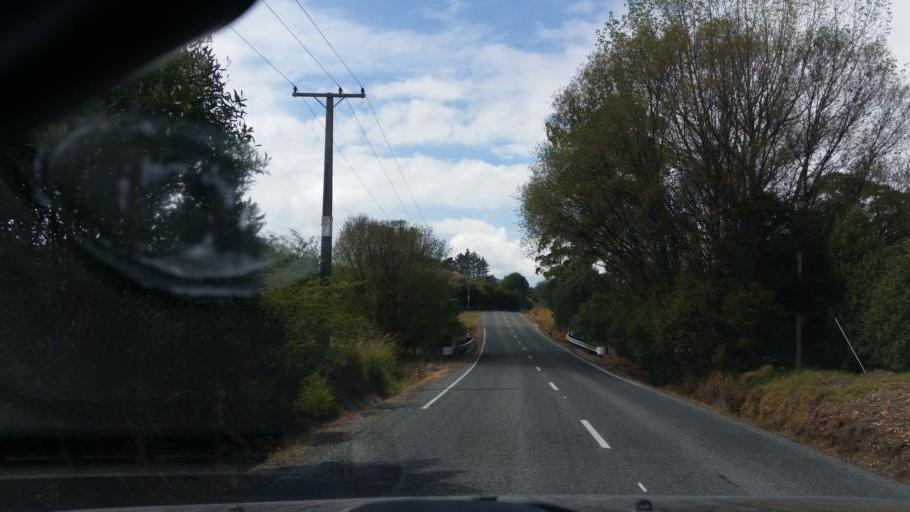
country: NZ
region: Auckland
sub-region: Auckland
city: Wellsford
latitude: -36.1230
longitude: 174.5554
